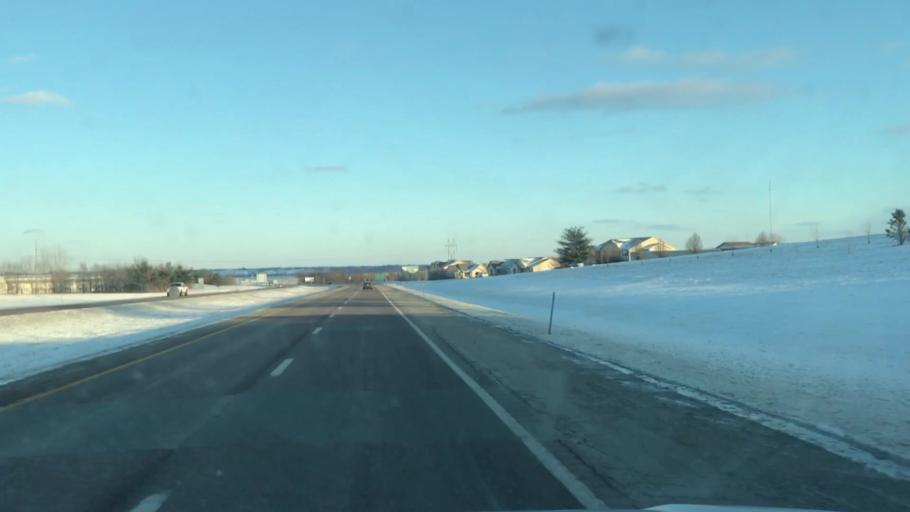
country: US
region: Missouri
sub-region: Buchanan County
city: Saint Joseph
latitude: 39.7493
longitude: -94.7675
